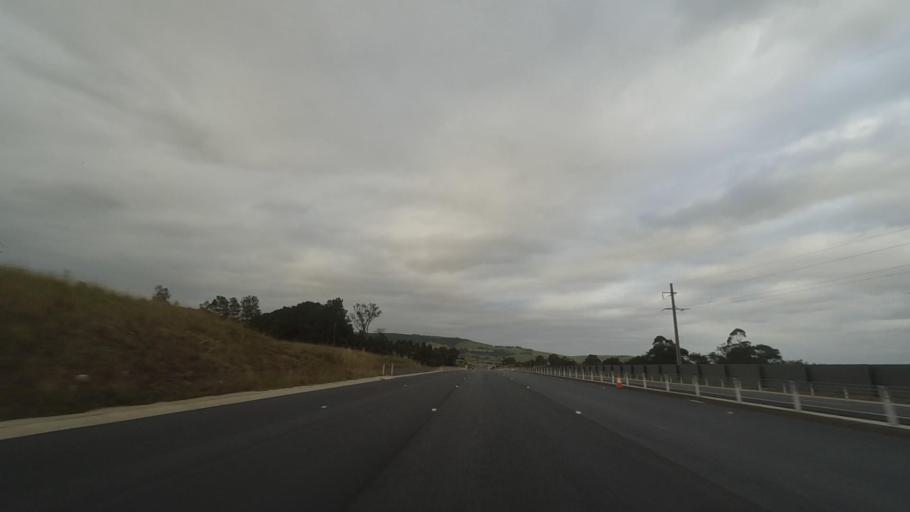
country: AU
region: New South Wales
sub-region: Kiama
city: Gerringong
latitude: -34.7392
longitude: 150.8208
